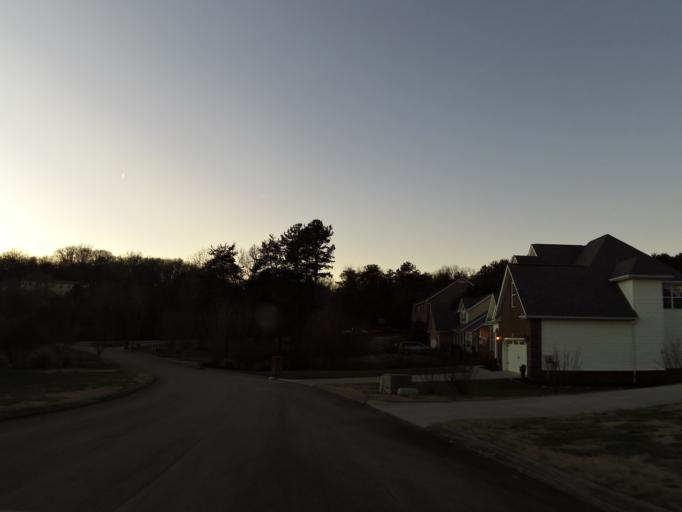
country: US
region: Tennessee
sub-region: Blount County
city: Eagleton Village
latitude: 35.8778
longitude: -83.9427
